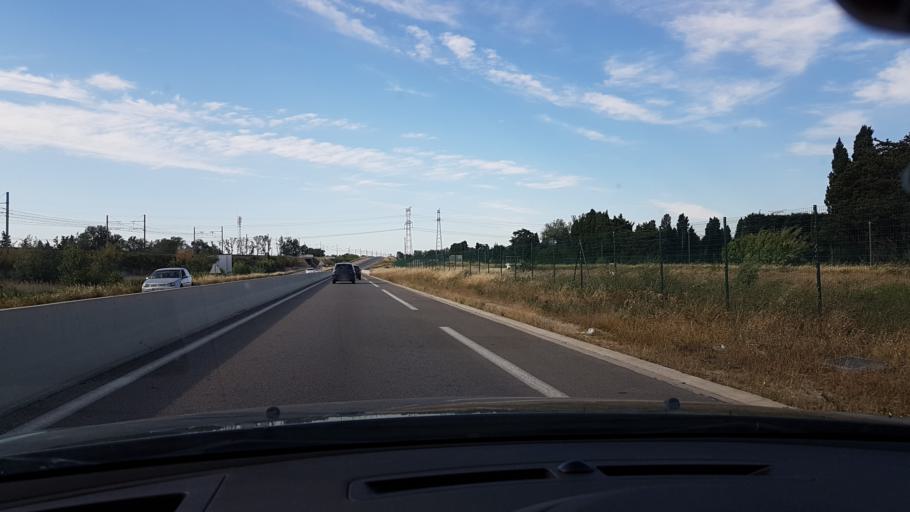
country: FR
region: Provence-Alpes-Cote d'Azur
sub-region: Departement des Bouches-du-Rhone
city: Rognonas
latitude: 43.9093
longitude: 4.7914
